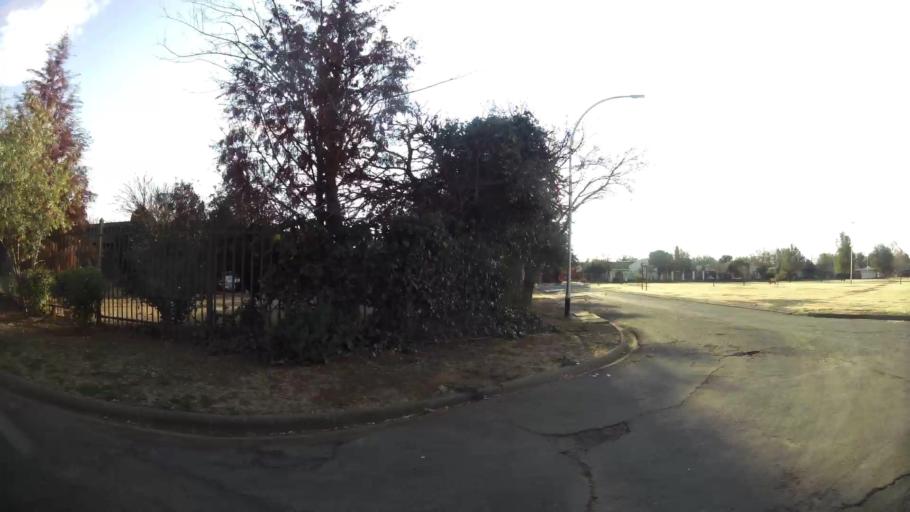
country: ZA
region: Orange Free State
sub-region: Mangaung Metropolitan Municipality
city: Bloemfontein
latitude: -29.1538
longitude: 26.1870
